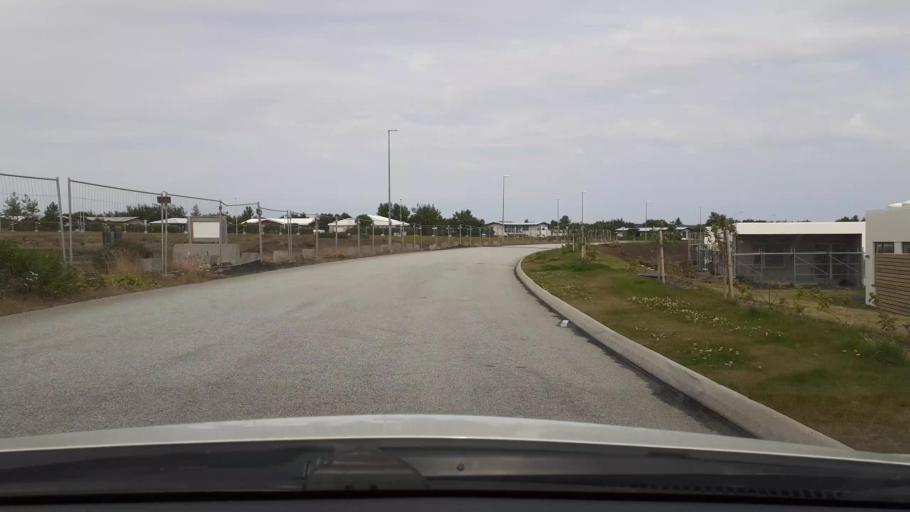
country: IS
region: Southern Peninsula
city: Reykjanesbaer
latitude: 63.9946
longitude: -22.5696
